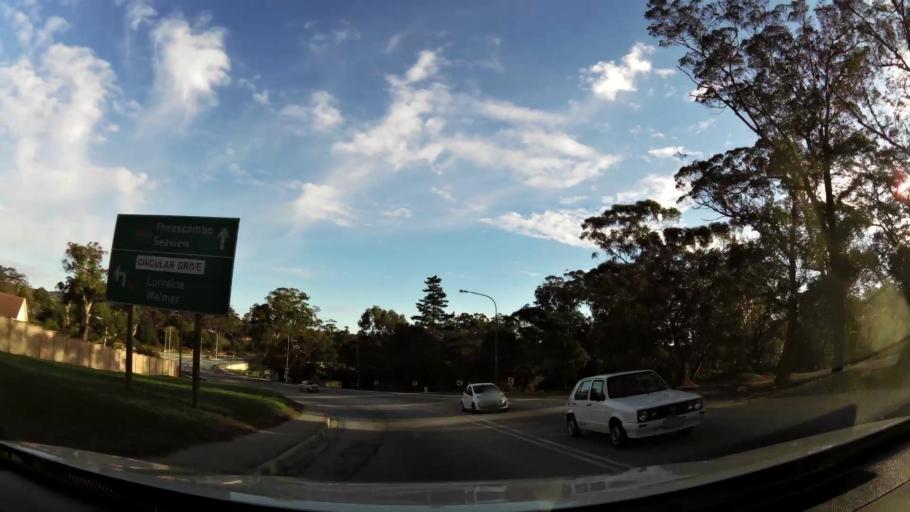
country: ZA
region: Eastern Cape
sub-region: Nelson Mandela Bay Metropolitan Municipality
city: Port Elizabeth
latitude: -33.9573
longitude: 25.5150
